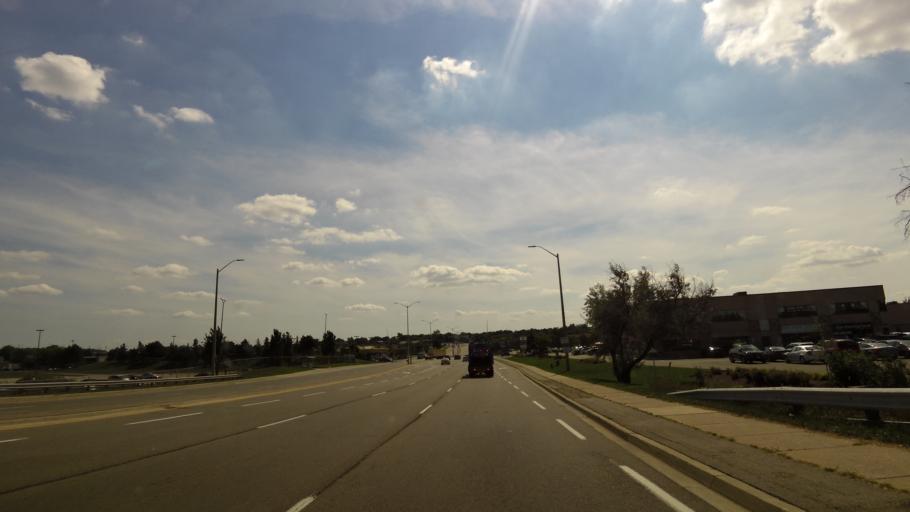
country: CA
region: Ontario
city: Mississauga
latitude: 43.5920
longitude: -79.7406
